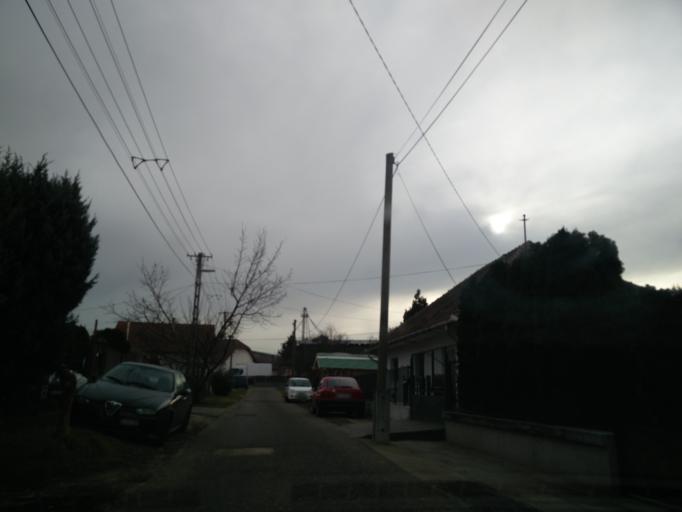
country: HU
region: Pest
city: Orbottyan
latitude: 47.6556
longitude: 19.2338
